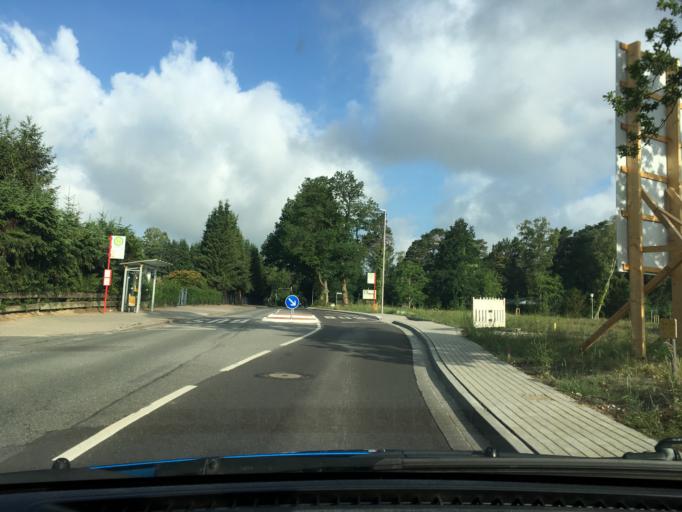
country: DE
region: Lower Saxony
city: Buchholz in der Nordheide
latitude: 53.3254
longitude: 9.8460
